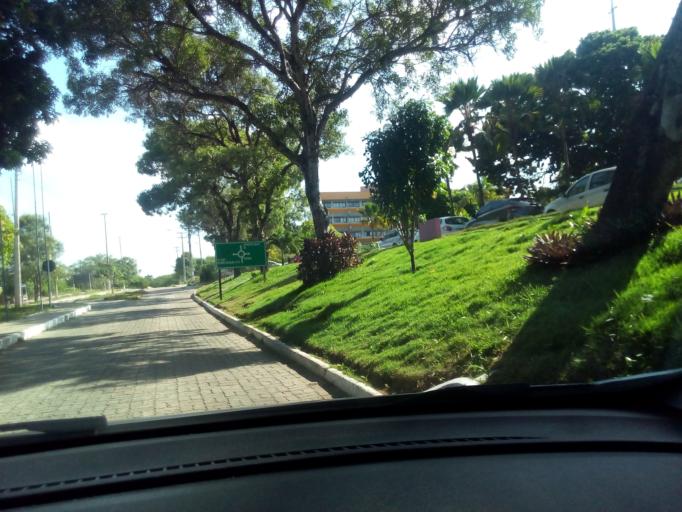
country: BR
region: Rio Grande do Norte
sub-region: Natal
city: Natal
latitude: -5.8396
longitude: -35.2011
